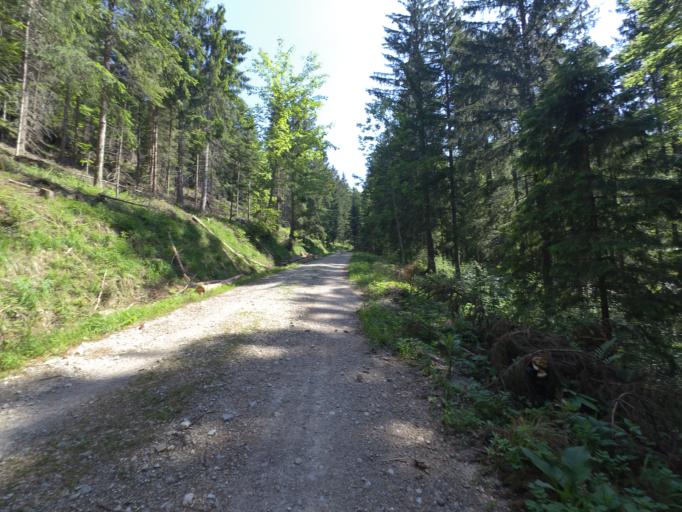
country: AT
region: Salzburg
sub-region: Politischer Bezirk Salzburg-Umgebung
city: Koppl
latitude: 47.7835
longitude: 13.1506
